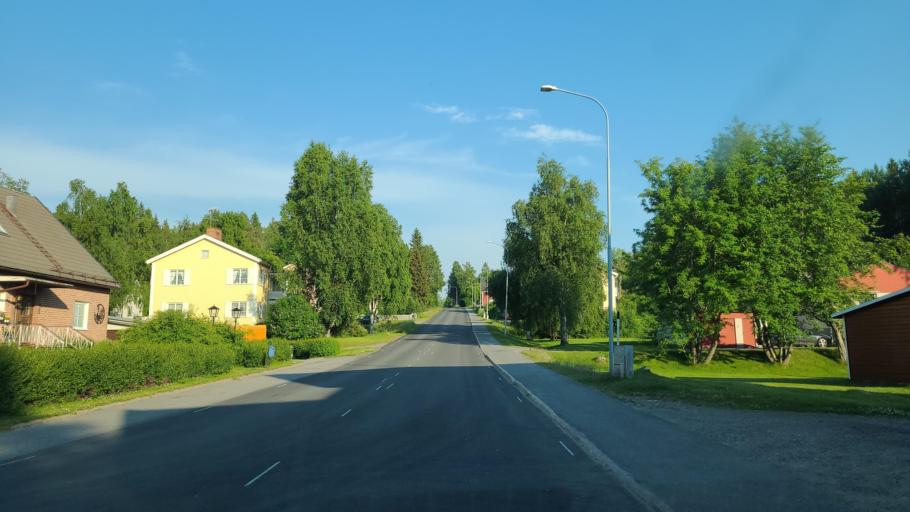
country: SE
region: Vaesterbotten
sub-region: Skelleftea Kommun
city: Burea
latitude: 64.3679
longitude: 21.3219
